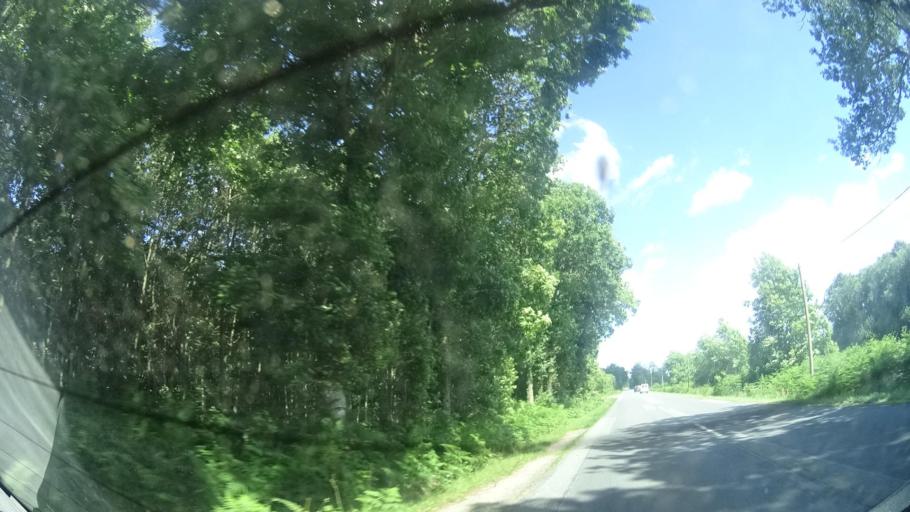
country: FR
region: Brittany
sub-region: Departement du Morbihan
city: Pluherlin
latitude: 47.6794
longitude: -2.4007
